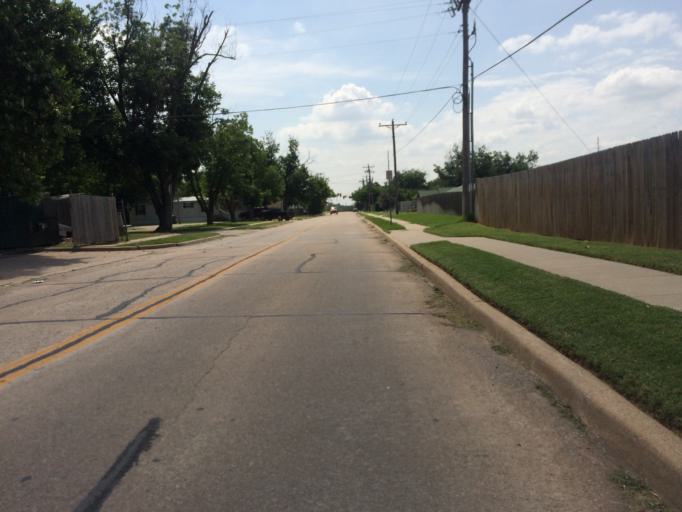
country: US
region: Oklahoma
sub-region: Cleveland County
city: Norman
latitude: 35.2076
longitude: -97.4742
